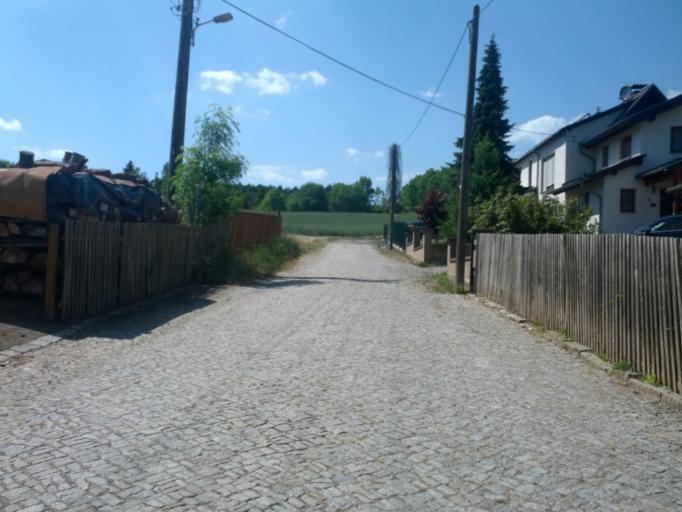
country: DE
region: Thuringia
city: Krauthausen
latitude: 50.9966
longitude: 10.2832
